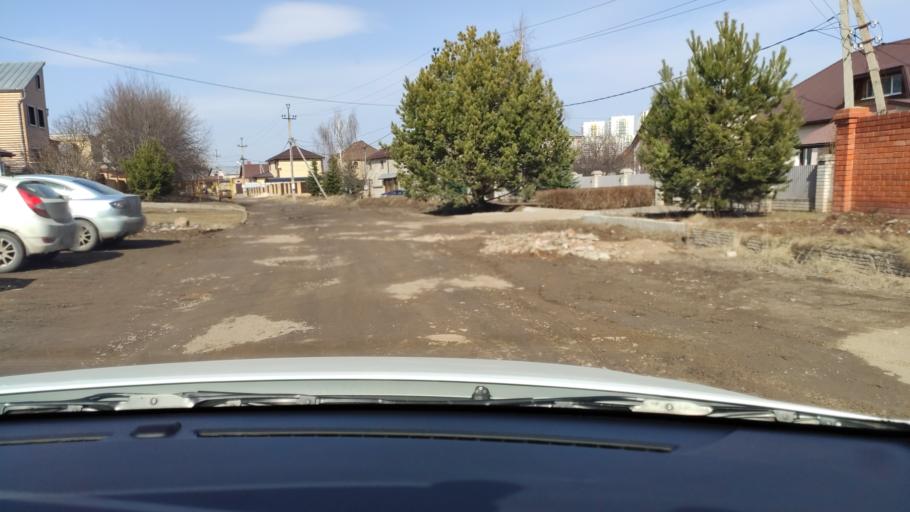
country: RU
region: Tatarstan
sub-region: Gorod Kazan'
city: Kazan
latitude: 55.7863
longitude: 49.2473
